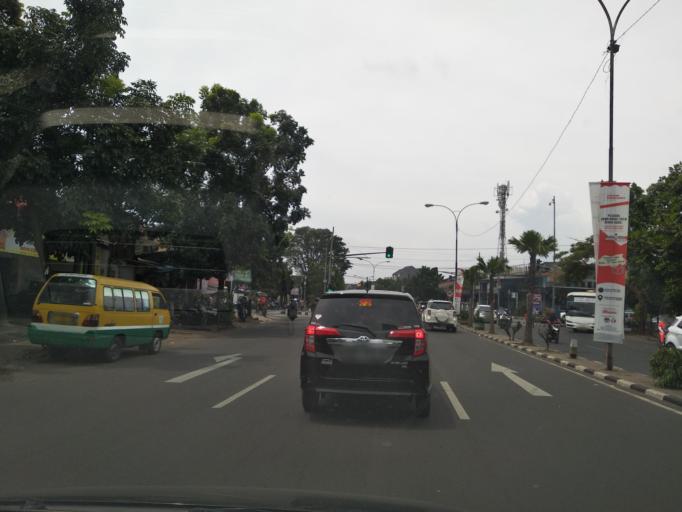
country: ID
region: West Java
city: Bandung
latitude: -6.9367
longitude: 107.5945
